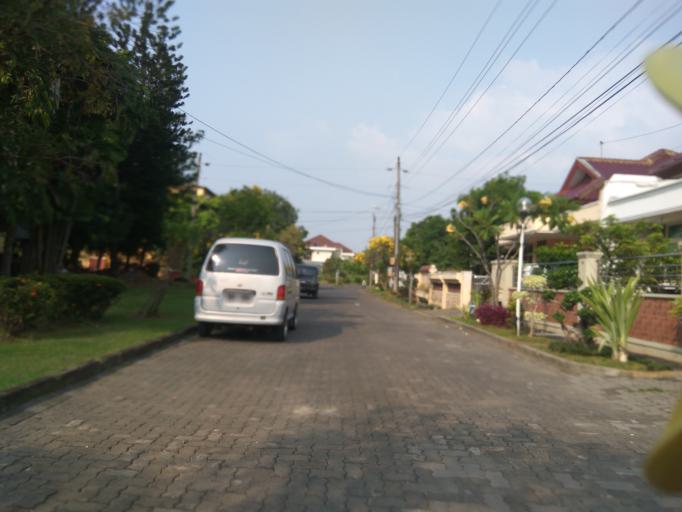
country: ID
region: Central Java
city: Semarang
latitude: -6.9646
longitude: 110.3853
